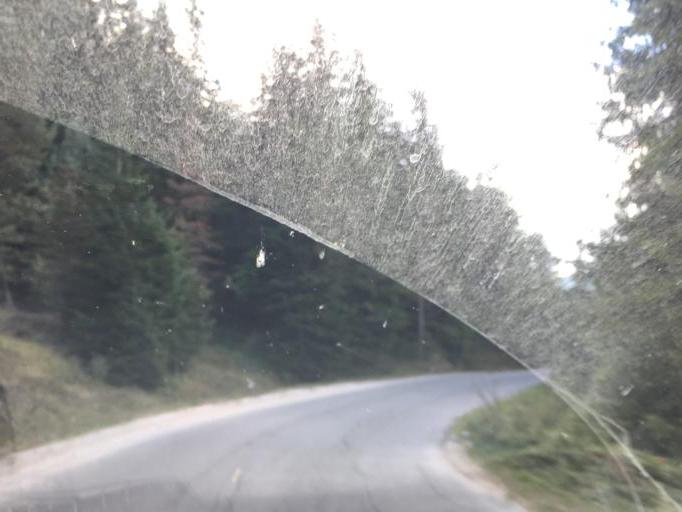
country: BG
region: Pazardzhik
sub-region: Obshtina Batak
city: Batak
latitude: 41.9232
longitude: 24.2828
